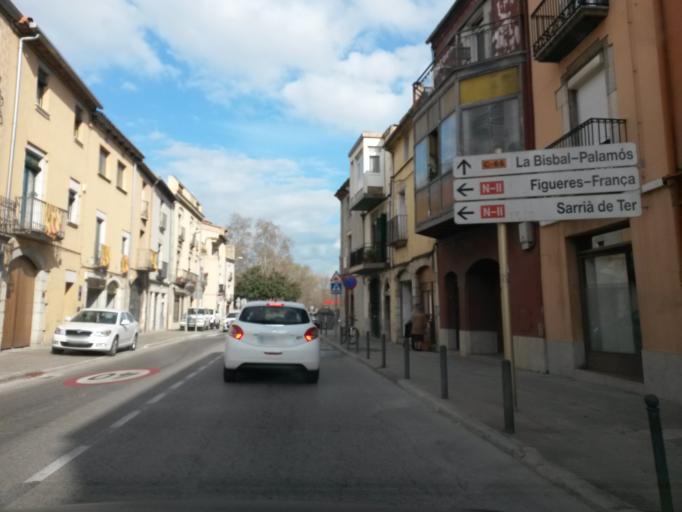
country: ES
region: Catalonia
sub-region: Provincia de Girona
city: Sarria de Ter
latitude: 42.0129
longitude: 2.8259
